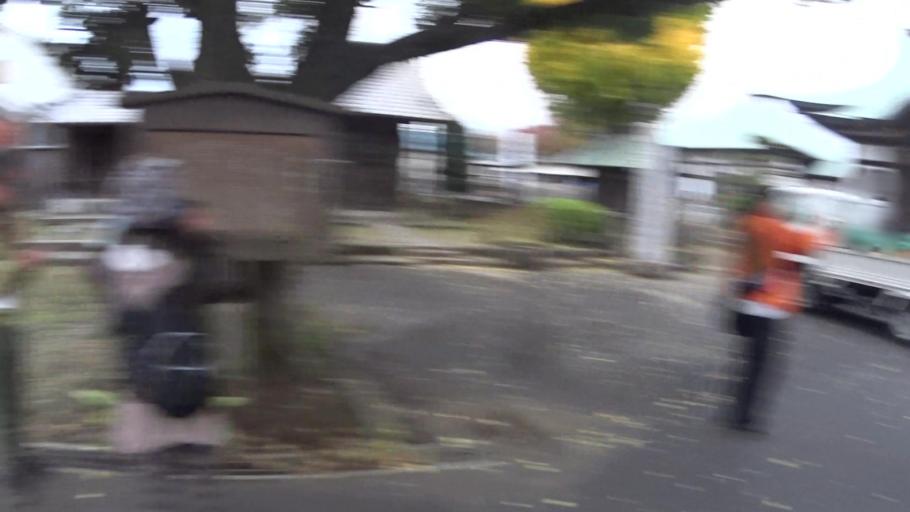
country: JP
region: Saitama
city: Yashio-shi
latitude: 35.8436
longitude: 139.8463
